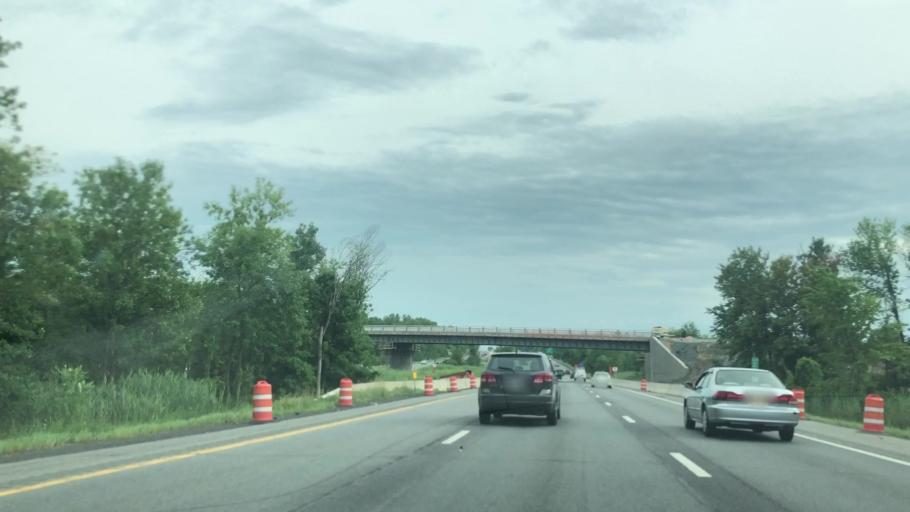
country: US
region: New York
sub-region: Saratoga County
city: Ballston Spa
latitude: 42.9970
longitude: -73.8039
